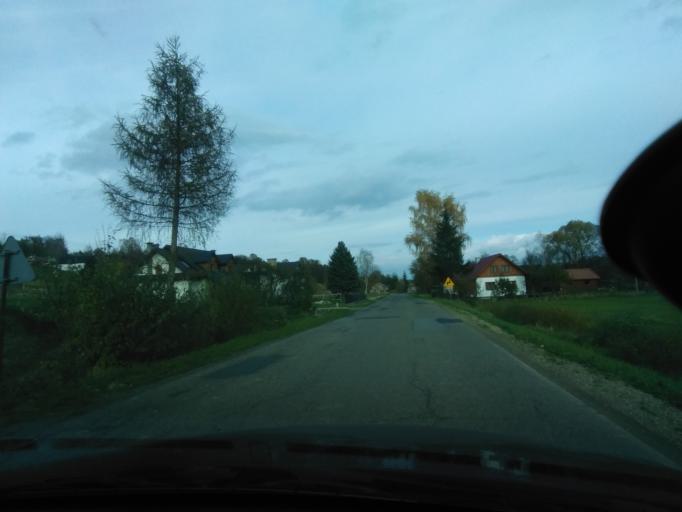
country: PL
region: Subcarpathian Voivodeship
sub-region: Powiat ropczycko-sedziszowski
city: Wielopole Skrzynskie
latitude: 49.9319
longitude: 21.5593
